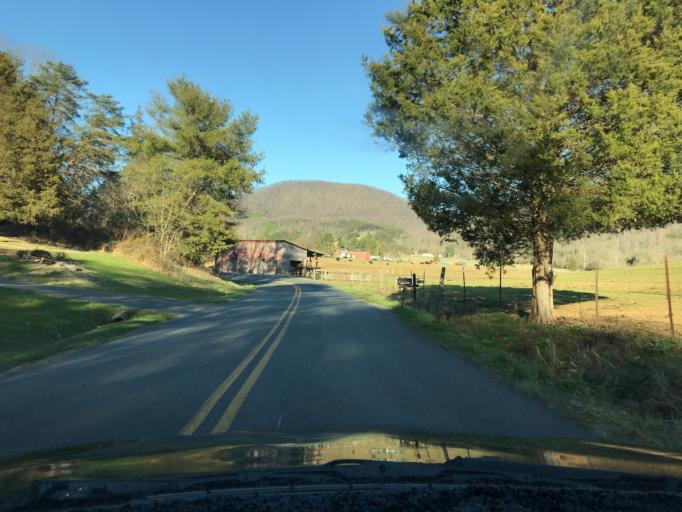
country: US
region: Virginia
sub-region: Botetourt County
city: Blue Ridge
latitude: 37.3984
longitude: -79.7036
